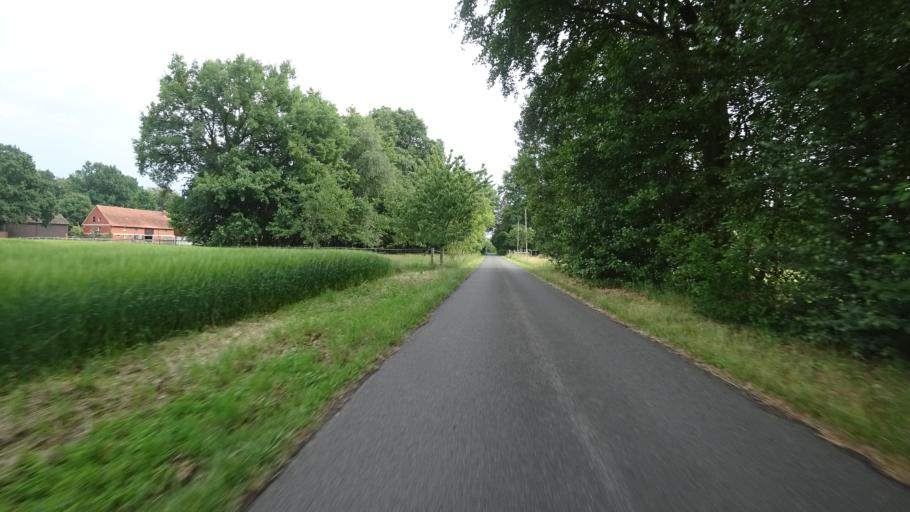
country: DE
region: North Rhine-Westphalia
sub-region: Regierungsbezirk Detmold
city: Guetersloh
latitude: 51.9505
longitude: 8.3612
